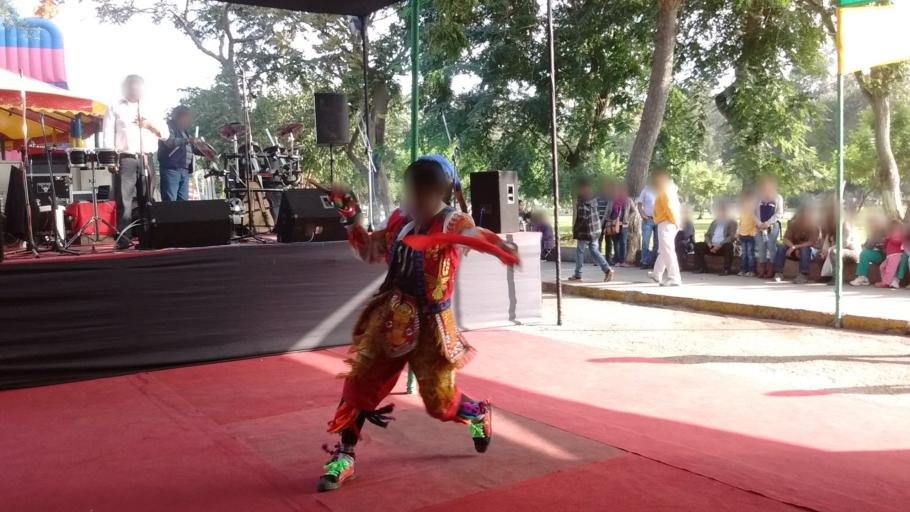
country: PE
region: Lima
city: Lima
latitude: -12.0669
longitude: -77.0401
